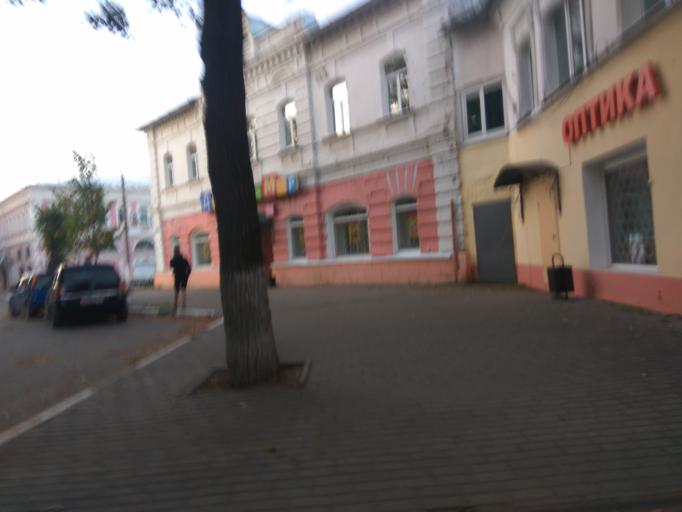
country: RU
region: Moskovskaya
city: Yegor'yevsk
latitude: 55.3832
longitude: 39.0370
